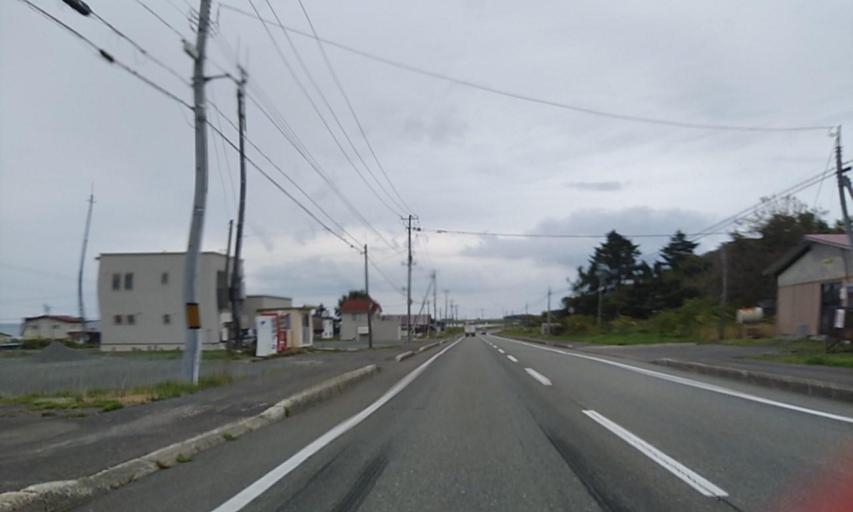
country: JP
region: Hokkaido
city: Nayoro
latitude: 45.0355
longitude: 142.5124
